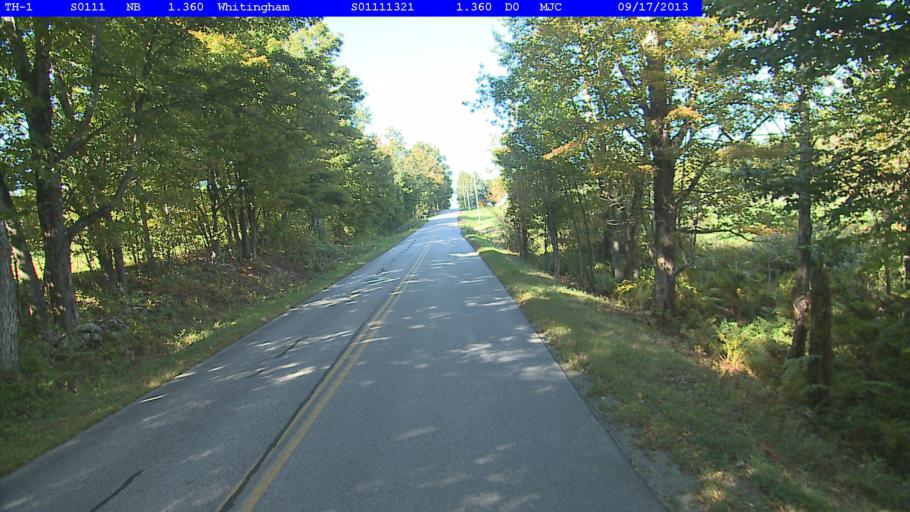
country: US
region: Massachusetts
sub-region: Franklin County
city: Charlemont
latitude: 42.7556
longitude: -72.8195
